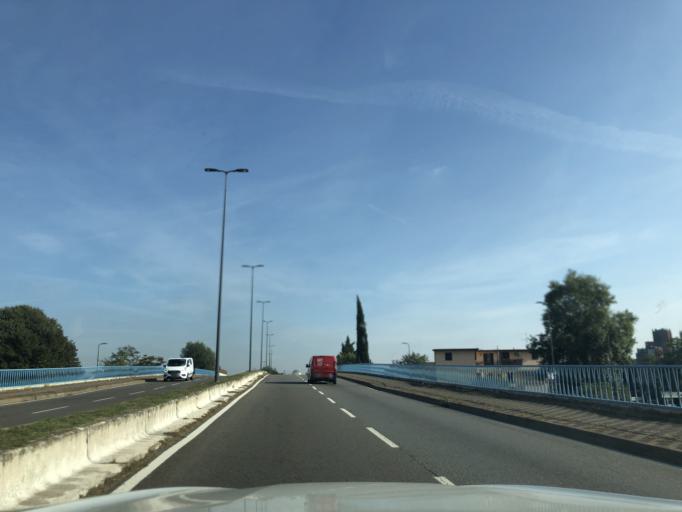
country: IT
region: Lombardy
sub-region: Citta metropolitana di Milano
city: Novate Milanese
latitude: 45.5130
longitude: 9.1590
